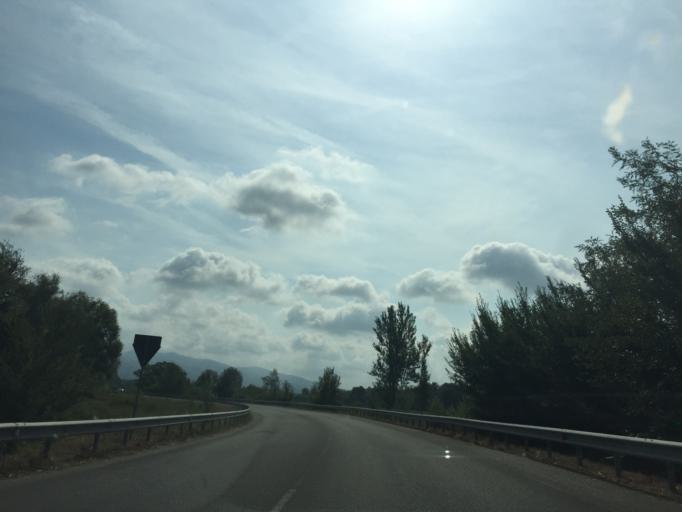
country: IT
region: Tuscany
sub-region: Provincia di Pistoia
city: San Rocco
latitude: 43.8135
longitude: 10.8524
